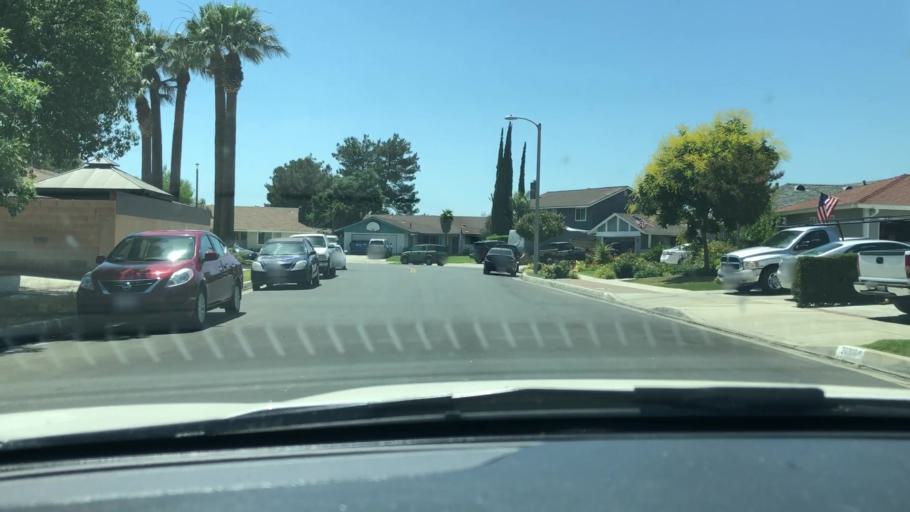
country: US
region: California
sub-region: Los Angeles County
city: Santa Clarita
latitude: 34.4266
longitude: -118.4901
